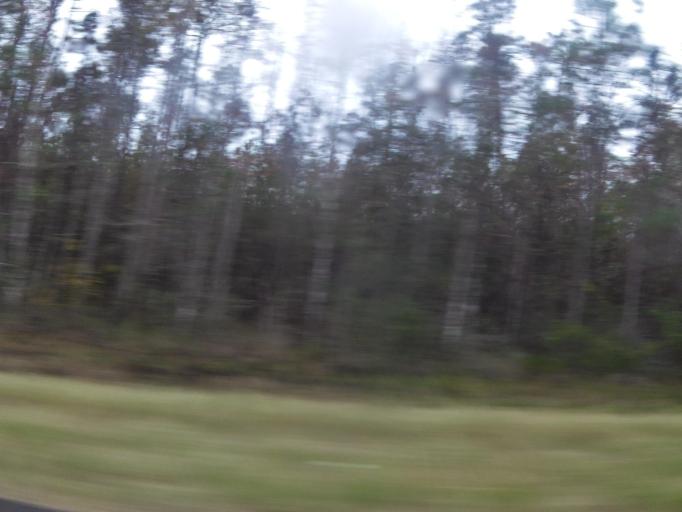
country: US
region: Georgia
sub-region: Charlton County
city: Folkston
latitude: 30.8957
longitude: -82.0556
